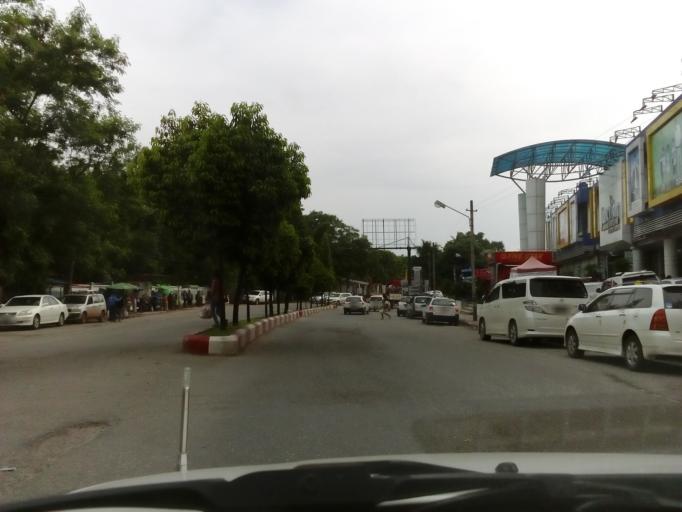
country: MM
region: Yangon
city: Yangon
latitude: 16.8652
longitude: 96.1414
